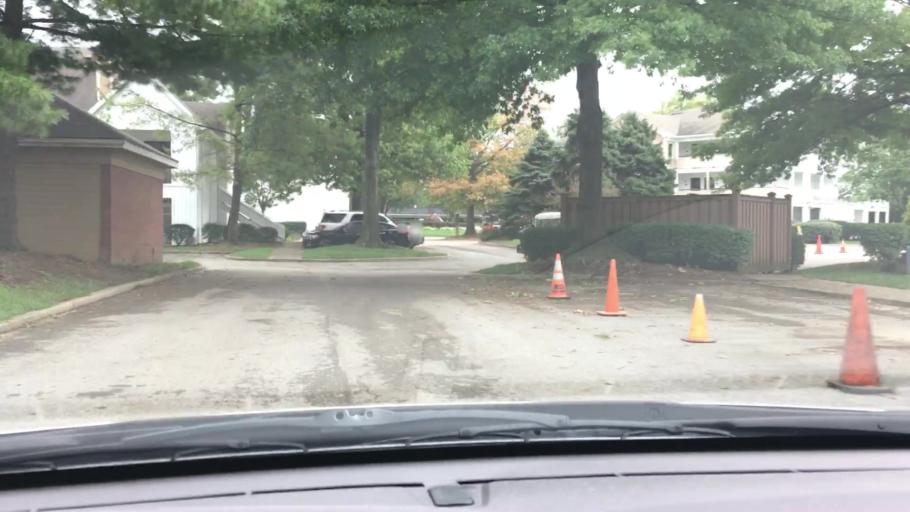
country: US
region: Kentucky
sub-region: Jefferson County
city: Beechwood Village
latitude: 38.2403
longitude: -85.6282
